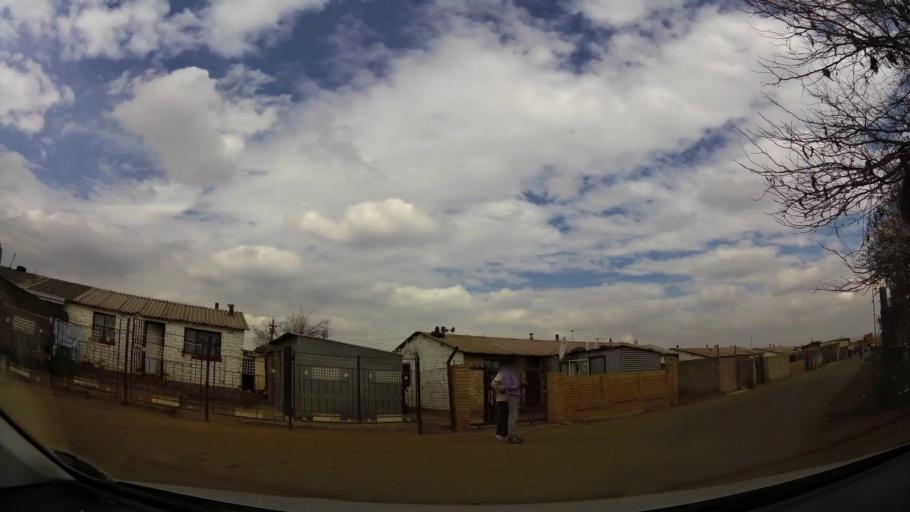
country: ZA
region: Gauteng
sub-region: City of Johannesburg Metropolitan Municipality
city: Soweto
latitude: -26.2709
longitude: 27.8535
